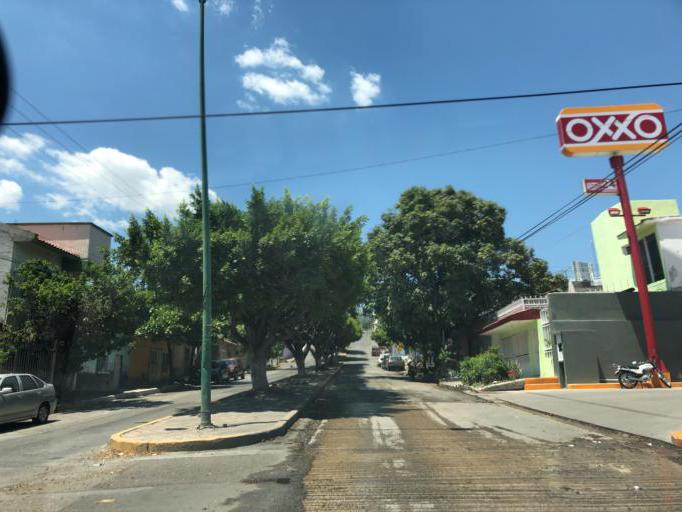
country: MX
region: Chiapas
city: Tuxtla Gutierrez
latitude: 16.7511
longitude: -93.1265
